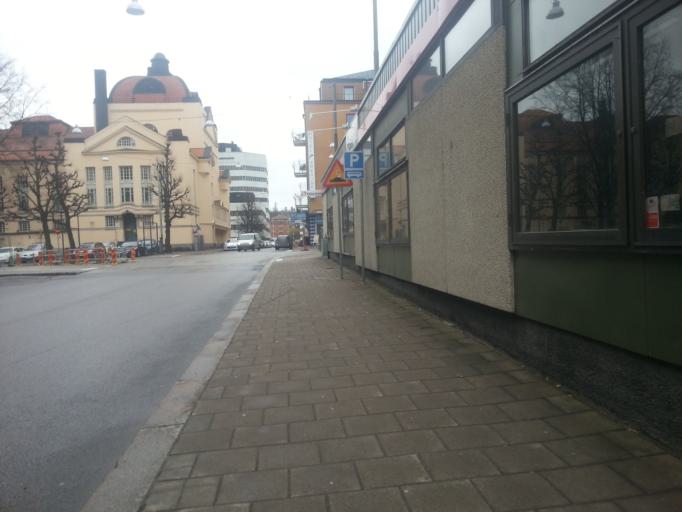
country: SE
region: OEstergoetland
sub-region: Norrkopings Kommun
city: Norrkoping
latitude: 58.5947
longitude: 16.1812
